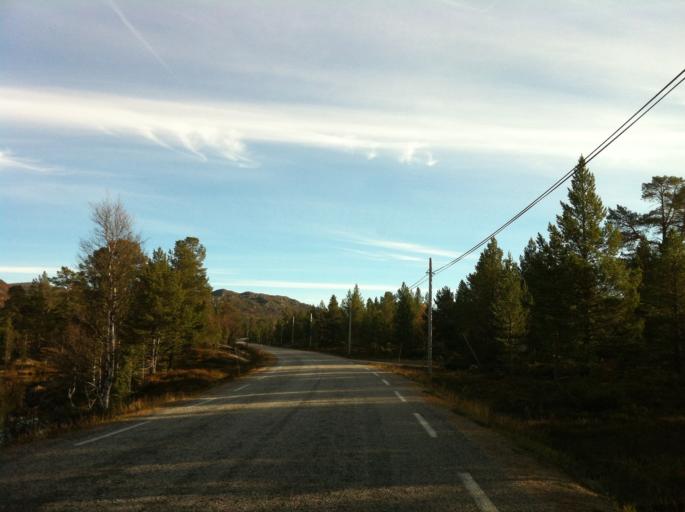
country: NO
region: Hedmark
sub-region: Engerdal
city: Engerdal
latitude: 62.1225
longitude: 12.0053
